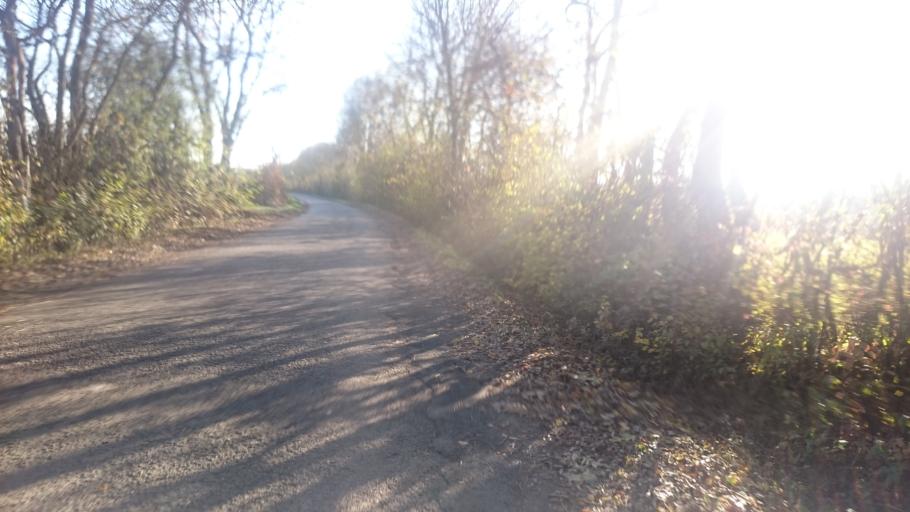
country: FR
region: Bourgogne
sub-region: Departement de Saone-et-Loire
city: Tournus
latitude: 46.5714
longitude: 4.9172
